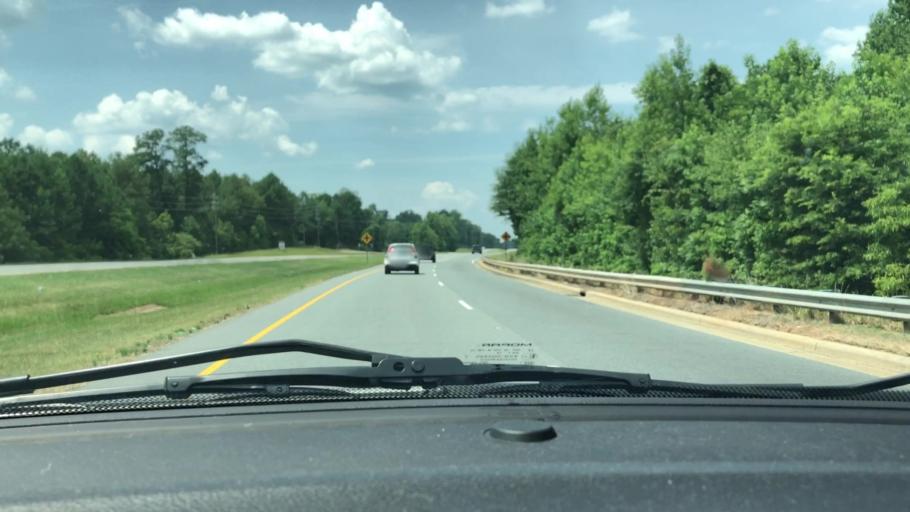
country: US
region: North Carolina
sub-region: Lee County
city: Sanford
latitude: 35.5020
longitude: -79.2051
